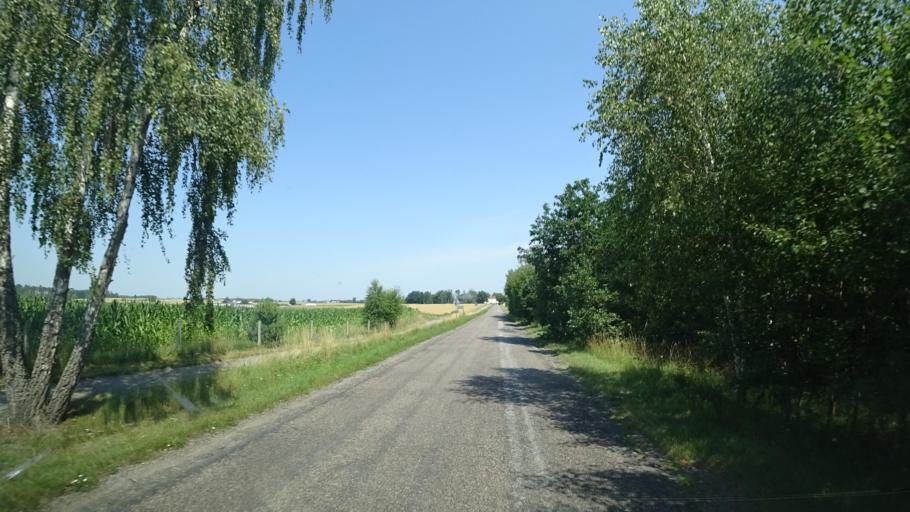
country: PL
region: Pomeranian Voivodeship
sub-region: Powiat chojnicki
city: Brusy
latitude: 53.8757
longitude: 17.6282
